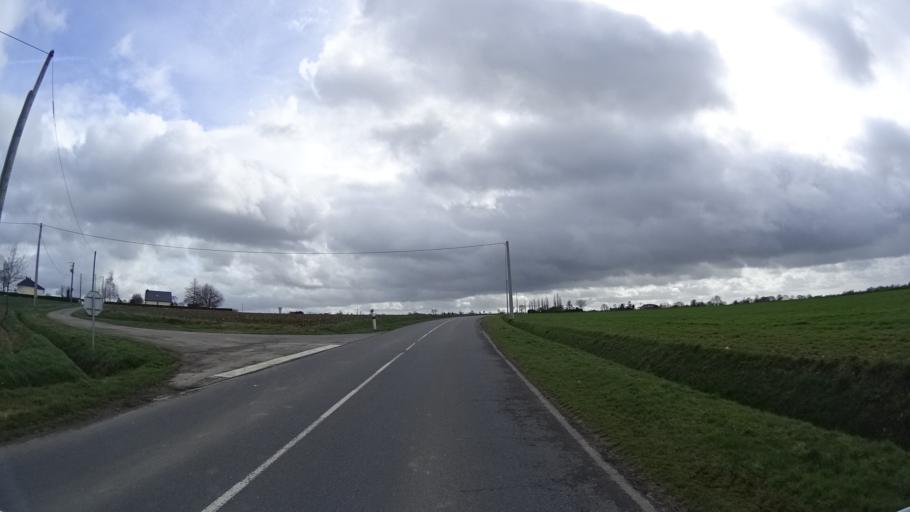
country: FR
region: Brittany
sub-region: Departement d'Ille-et-Vilaine
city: Romille
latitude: 48.1986
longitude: -1.8704
